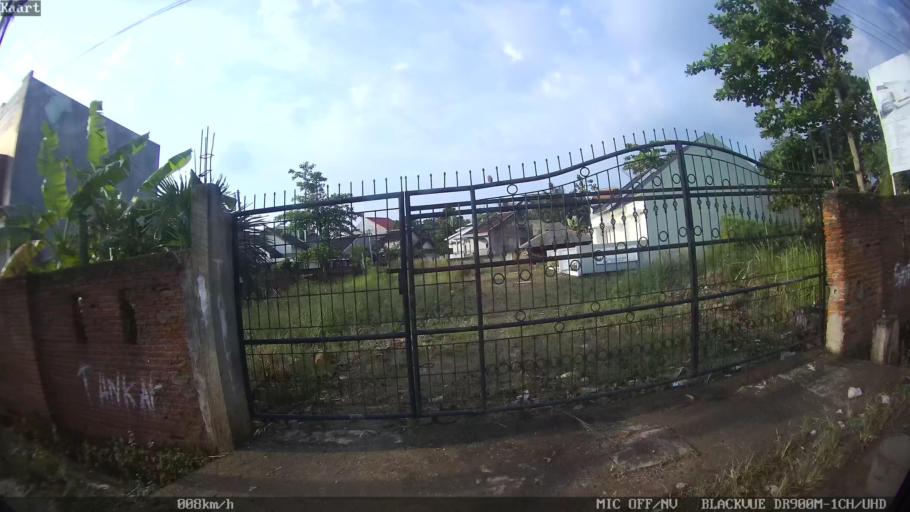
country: ID
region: Lampung
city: Kedaton
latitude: -5.3885
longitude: 105.3207
